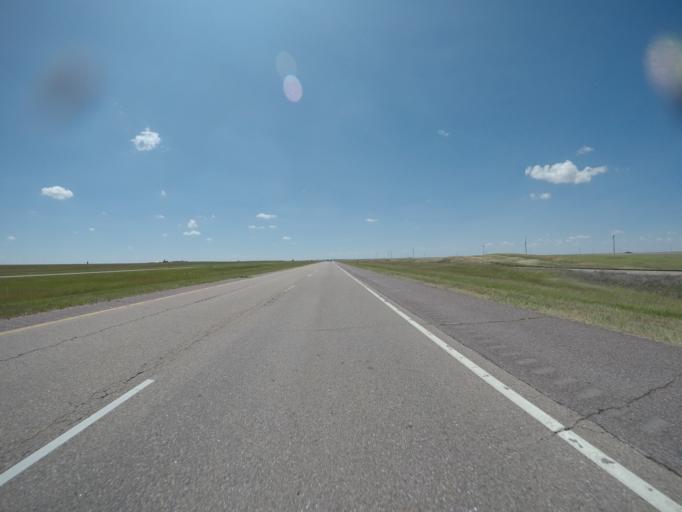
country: US
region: Colorado
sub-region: Lincoln County
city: Hugo
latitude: 39.2805
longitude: -103.3644
